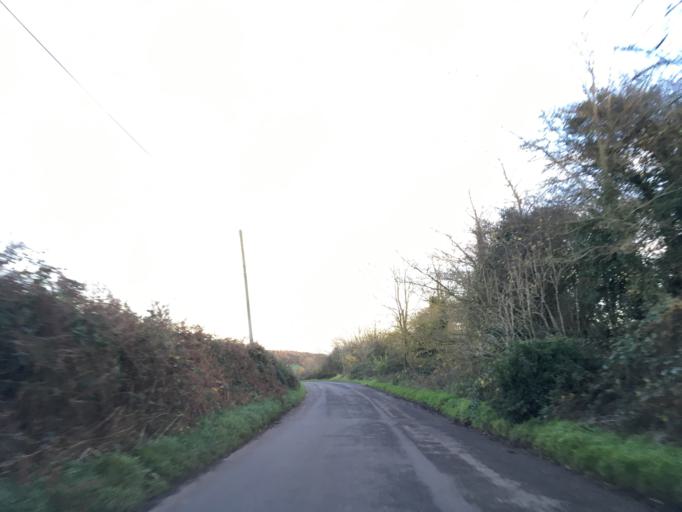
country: GB
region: England
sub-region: South Gloucestershire
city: Tytherington
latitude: 51.6095
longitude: -2.4763
